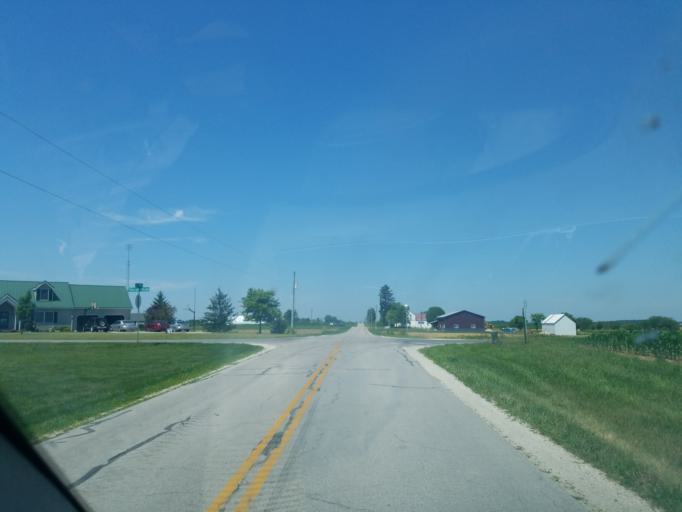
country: US
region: Ohio
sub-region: Mercer County
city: Saint Henry
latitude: 40.4506
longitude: -84.7076
